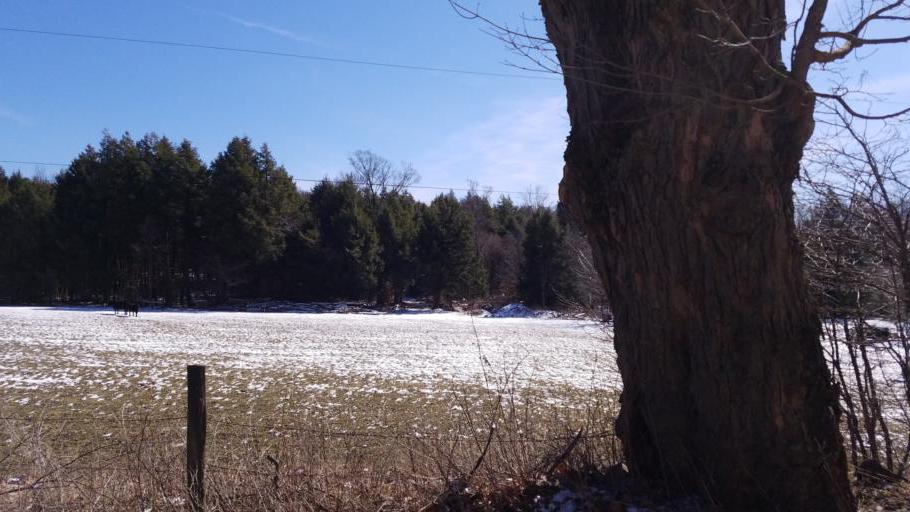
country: US
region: Pennsylvania
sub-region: Tioga County
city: Westfield
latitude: 41.9319
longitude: -77.7498
